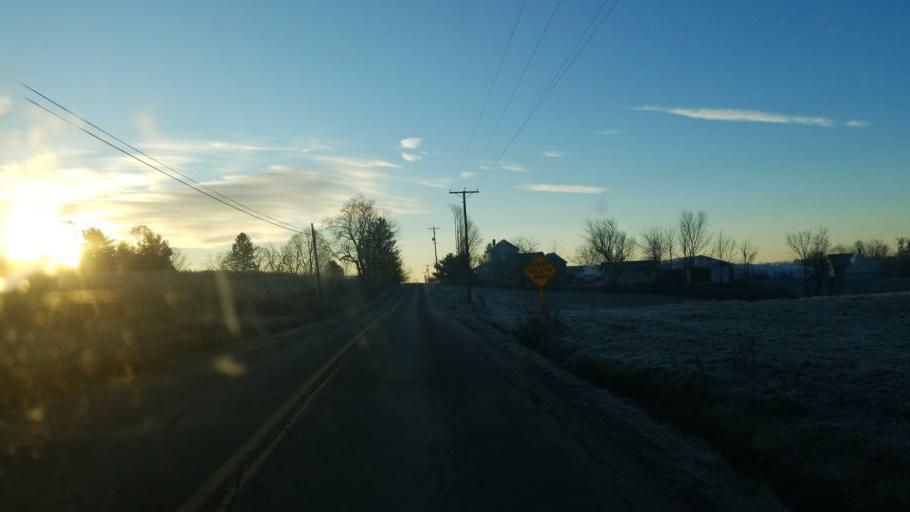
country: US
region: Ohio
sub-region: Holmes County
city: Millersburg
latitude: 40.6200
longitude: -81.8287
